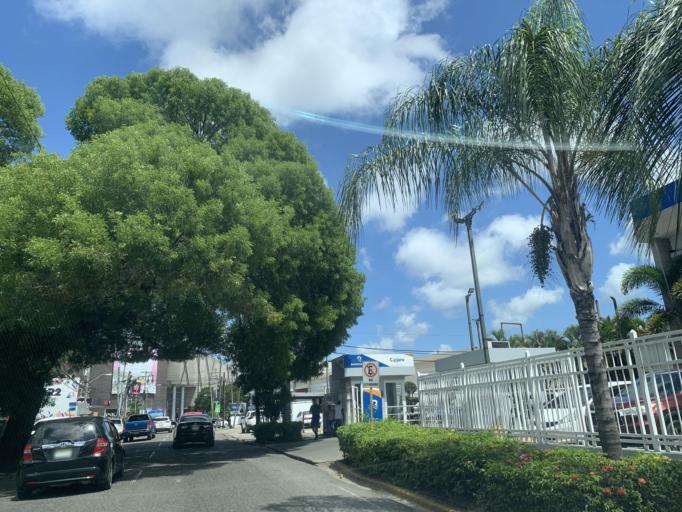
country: DO
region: Nacional
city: San Carlos
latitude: 18.4825
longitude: -69.9092
